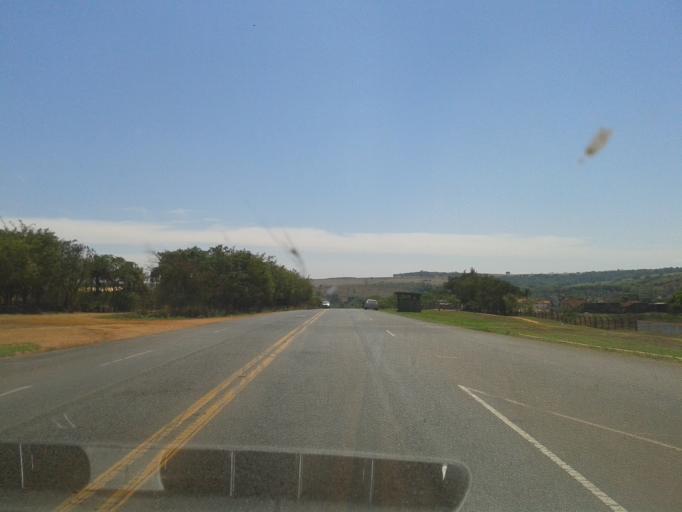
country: BR
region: Minas Gerais
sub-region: Sacramento
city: Sacramento
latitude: -19.3087
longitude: -47.5368
